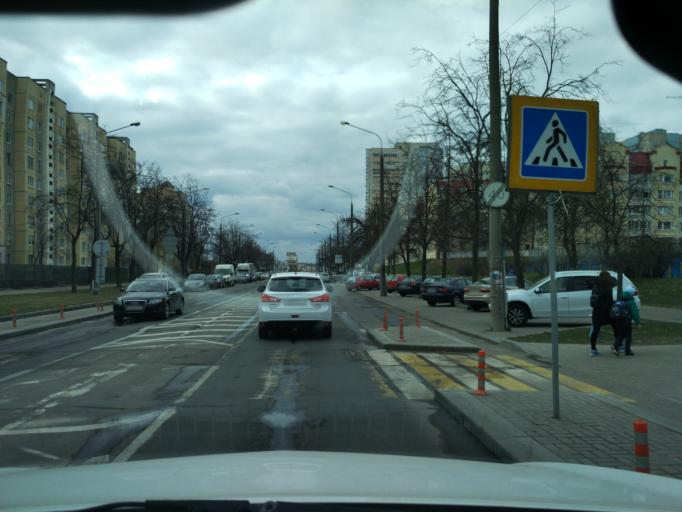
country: BY
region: Minsk
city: Minsk
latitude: 53.9341
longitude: 27.5870
